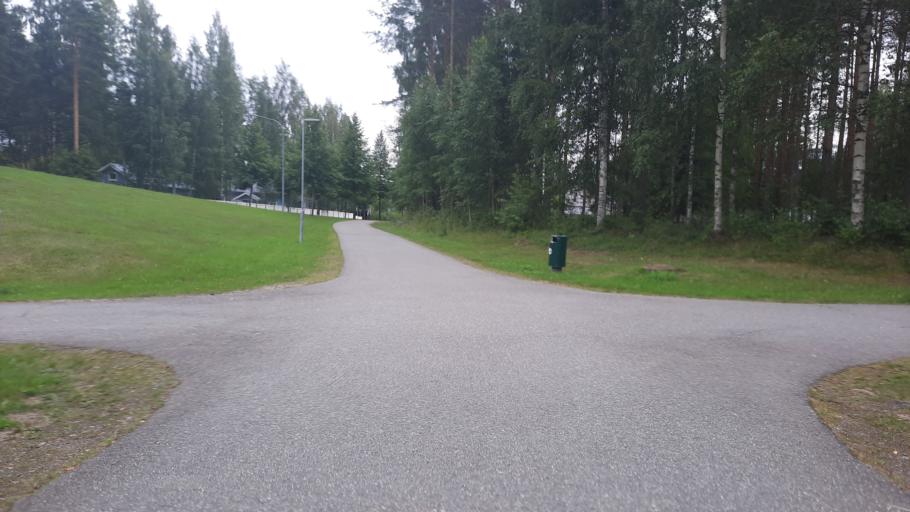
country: FI
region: North Karelia
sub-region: Joensuu
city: Joensuu
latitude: 62.6221
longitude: 29.8573
